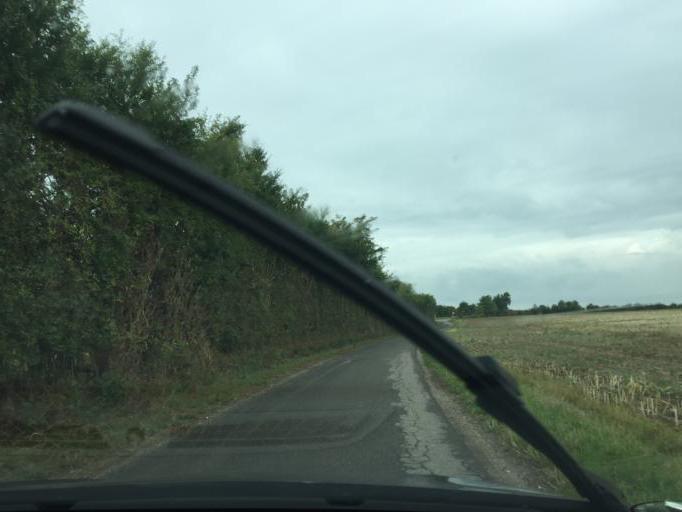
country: DK
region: South Denmark
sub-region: Assens Kommune
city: Harby
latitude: 55.2069
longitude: 10.0156
